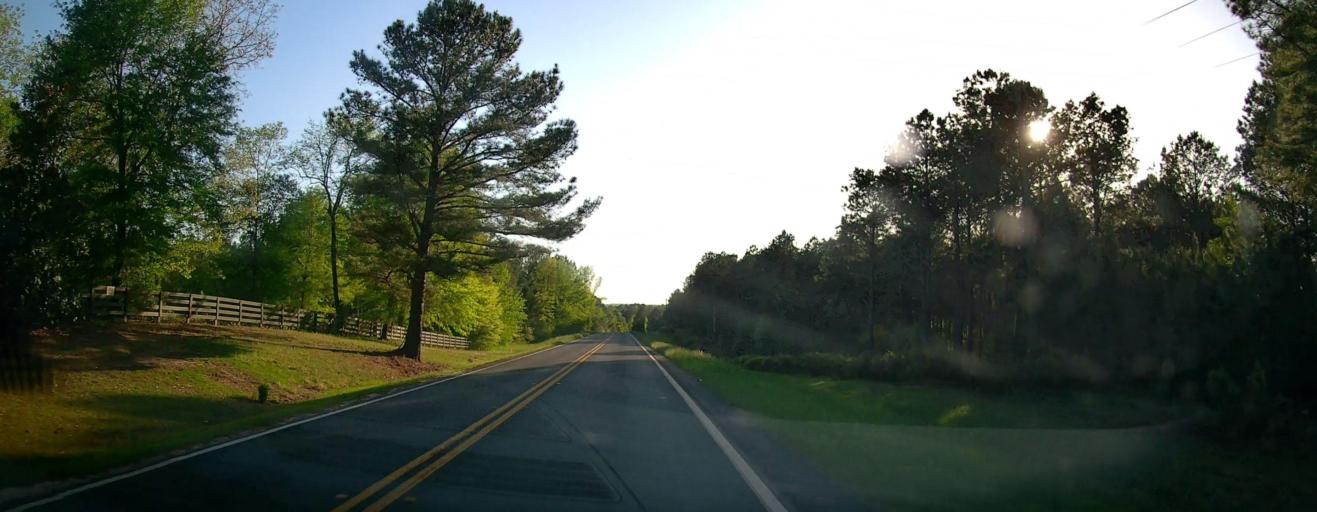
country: US
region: Georgia
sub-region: Schley County
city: Ellaville
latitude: 32.3198
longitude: -84.2455
